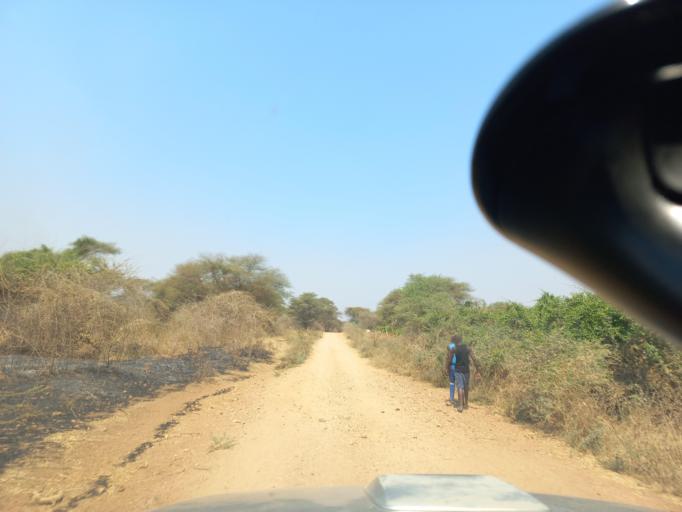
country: ZW
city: Chirundu
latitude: -15.9409
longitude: 28.8243
